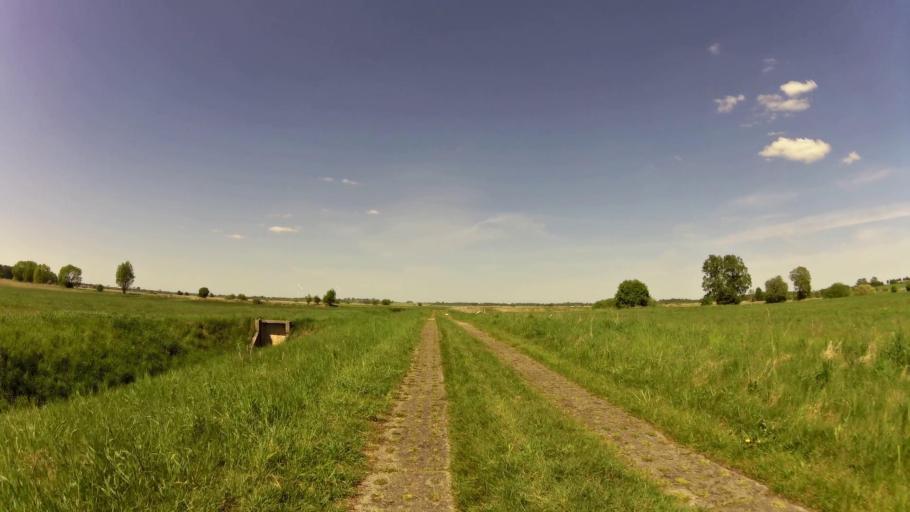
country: PL
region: West Pomeranian Voivodeship
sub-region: Powiat bialogardzki
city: Bialogard
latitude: 53.9990
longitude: 16.0445
